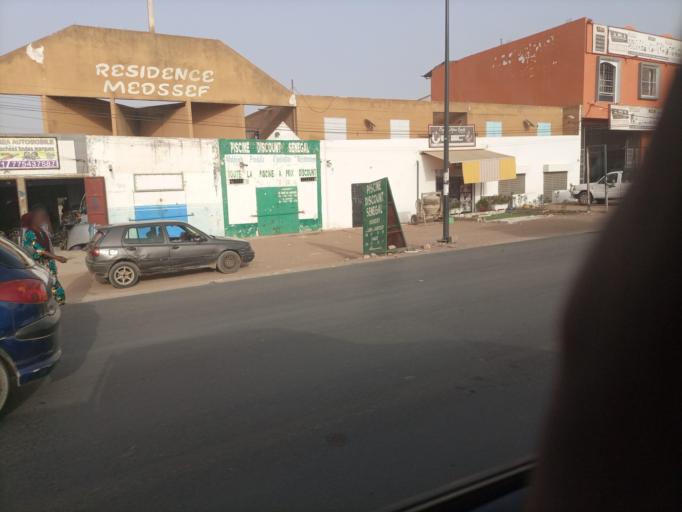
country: SN
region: Thies
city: Nguekhokh
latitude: 14.4413
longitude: -16.9790
